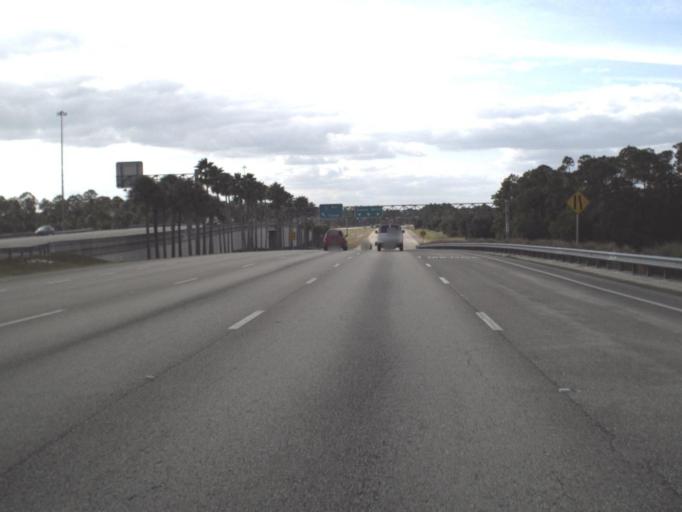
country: US
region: Florida
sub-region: Osceola County
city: Celebration
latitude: 28.3458
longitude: -81.5344
